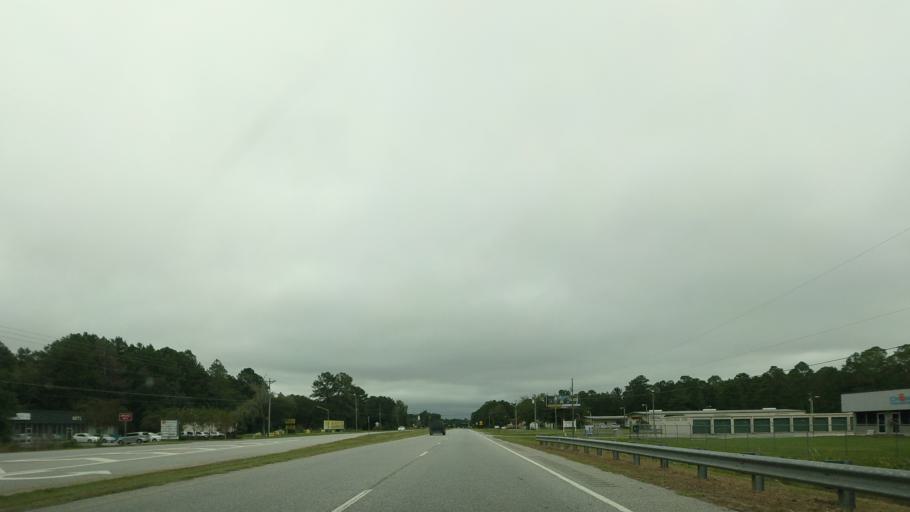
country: US
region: Georgia
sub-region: Lowndes County
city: Valdosta
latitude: 30.8824
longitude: -83.2558
